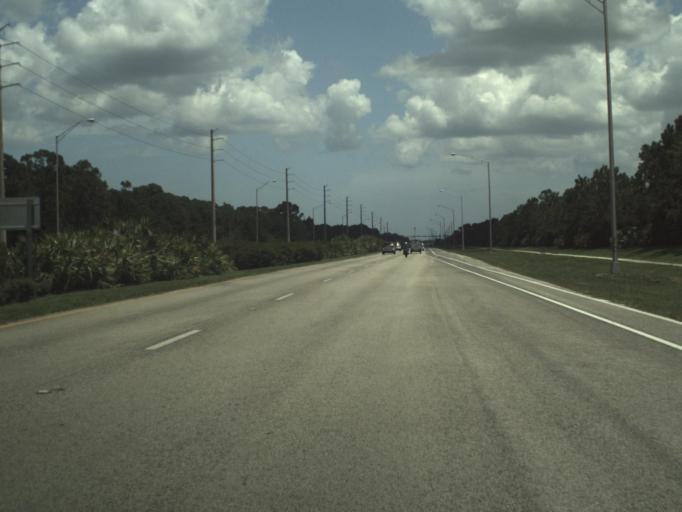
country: US
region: Florida
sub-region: Martin County
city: Port Salerno
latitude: 27.1152
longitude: -80.1761
